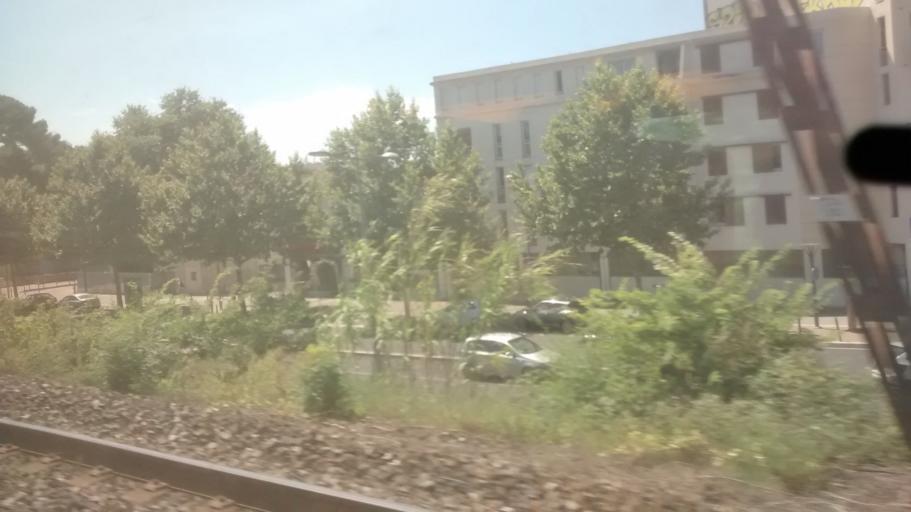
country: FR
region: Languedoc-Roussillon
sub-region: Departement de l'Herault
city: Montpellier
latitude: 43.6167
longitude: 3.8856
